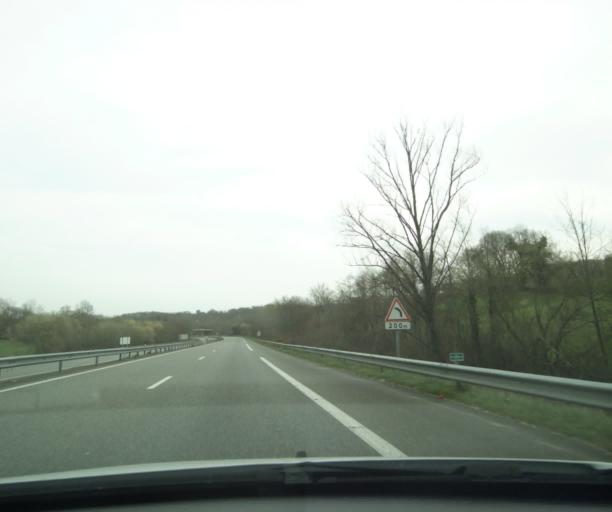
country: FR
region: Aquitaine
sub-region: Departement des Pyrenees-Atlantiques
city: Briscous
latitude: 43.4491
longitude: -1.3244
